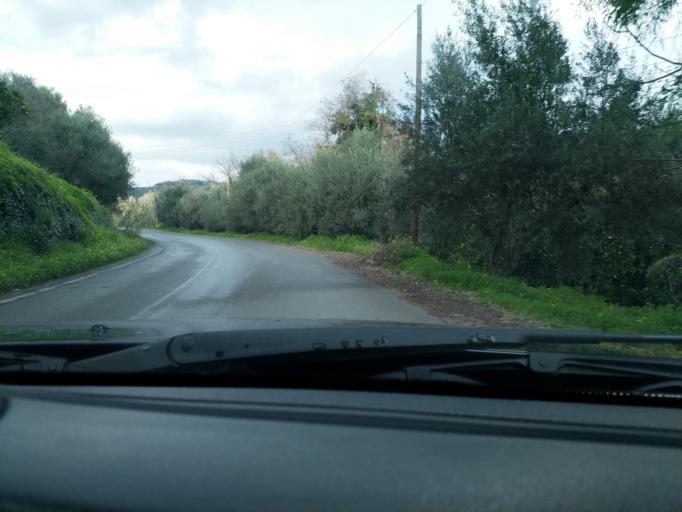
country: GR
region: Crete
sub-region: Nomos Chanias
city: Agia Marina
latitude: 35.4950
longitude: 23.9062
